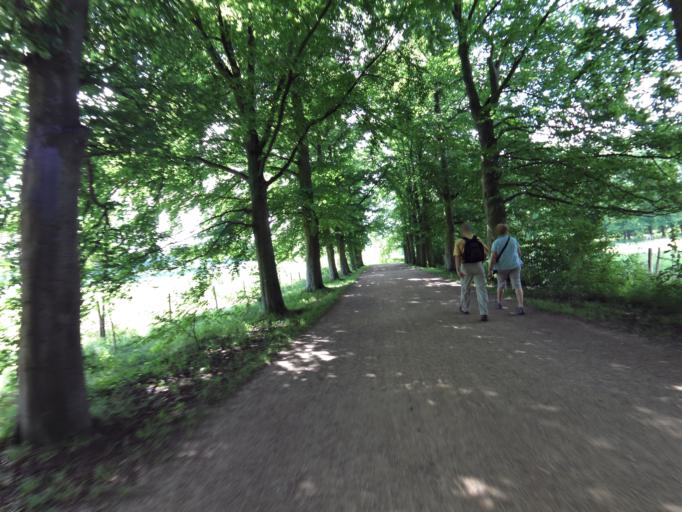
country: NL
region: Limburg
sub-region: Valkenburg aan de Geul
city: Schin op Geul
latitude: 50.8567
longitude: 5.8525
